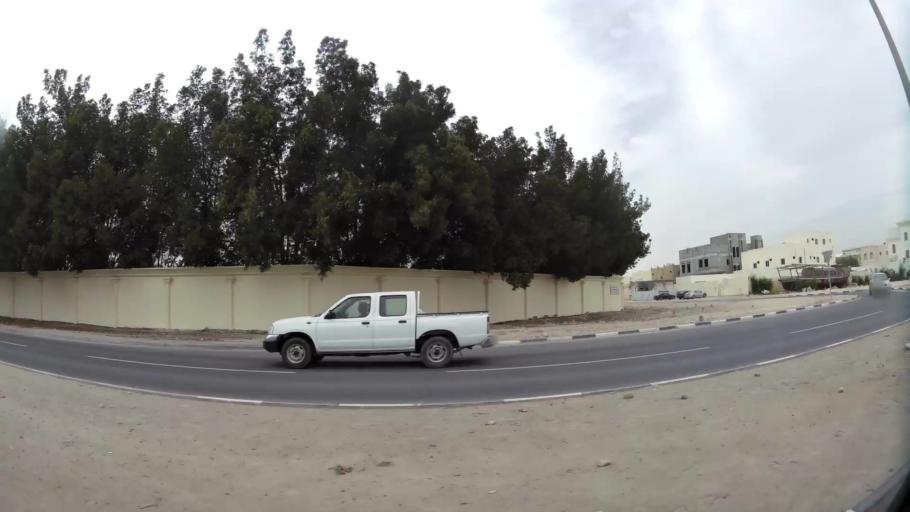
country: QA
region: Baladiyat ar Rayyan
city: Ar Rayyan
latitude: 25.2247
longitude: 51.4556
